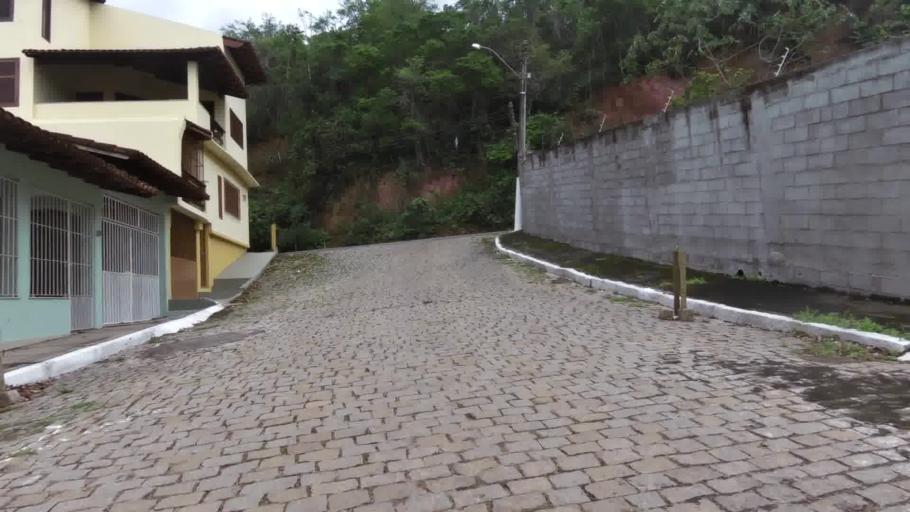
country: BR
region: Espirito Santo
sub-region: Marataizes
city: Marataizes
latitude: -21.0410
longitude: -40.8249
